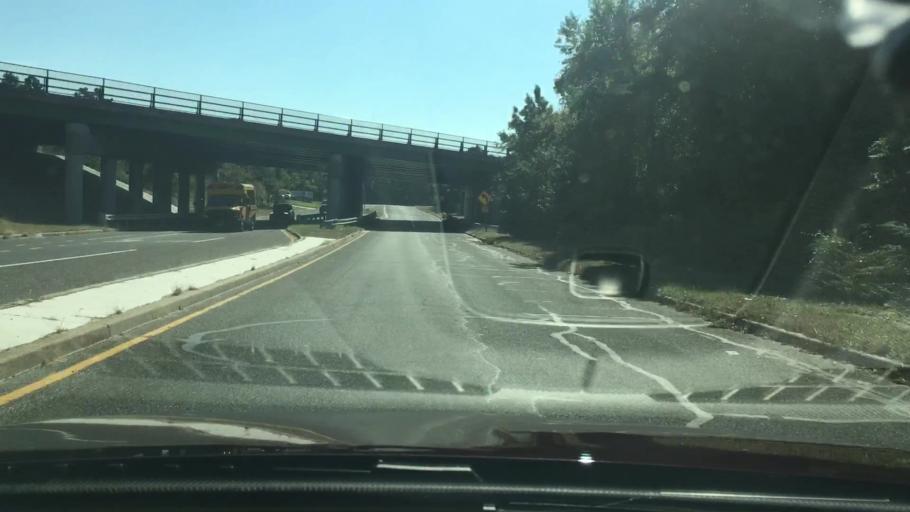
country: US
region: New York
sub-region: Suffolk County
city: Holtsville
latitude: 40.7906
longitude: -73.0433
